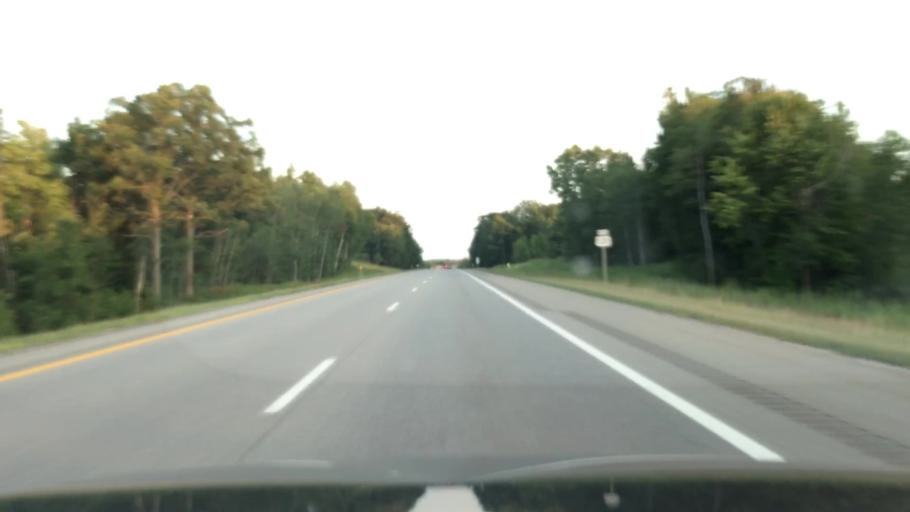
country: US
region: Michigan
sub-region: Montcalm County
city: Howard City
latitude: 43.4819
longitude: -85.4820
